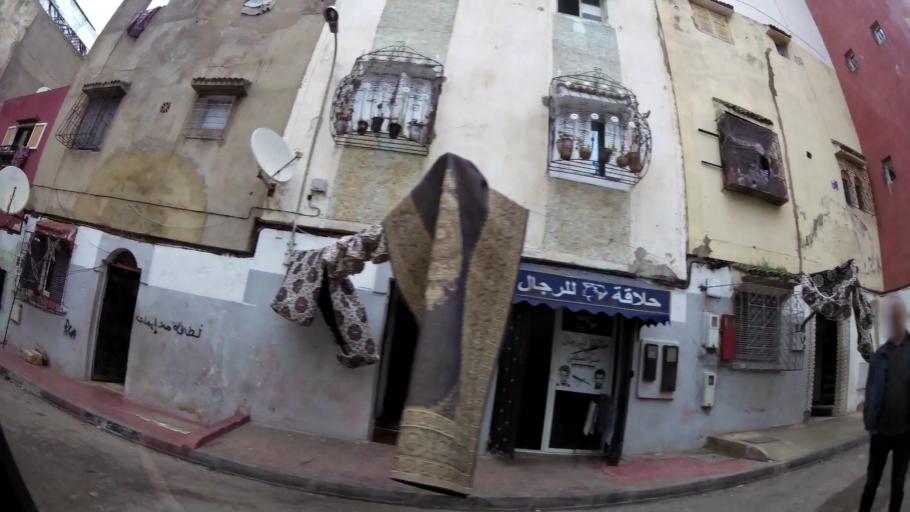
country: MA
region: Grand Casablanca
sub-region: Mediouna
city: Tit Mellil
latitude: 33.5694
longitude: -7.5419
